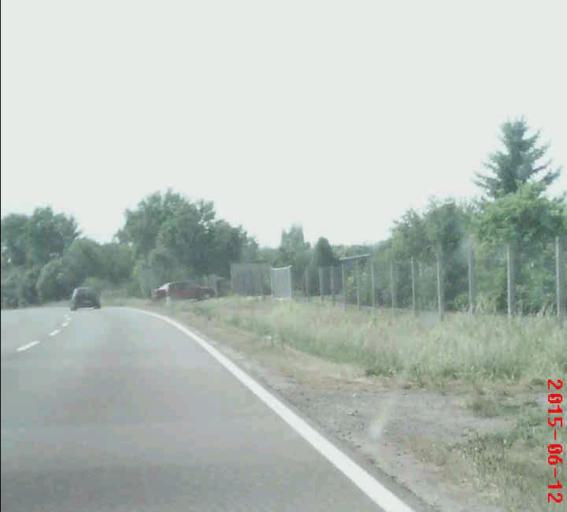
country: DE
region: Saxony-Anhalt
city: Rossla
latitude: 51.4649
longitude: 11.0861
